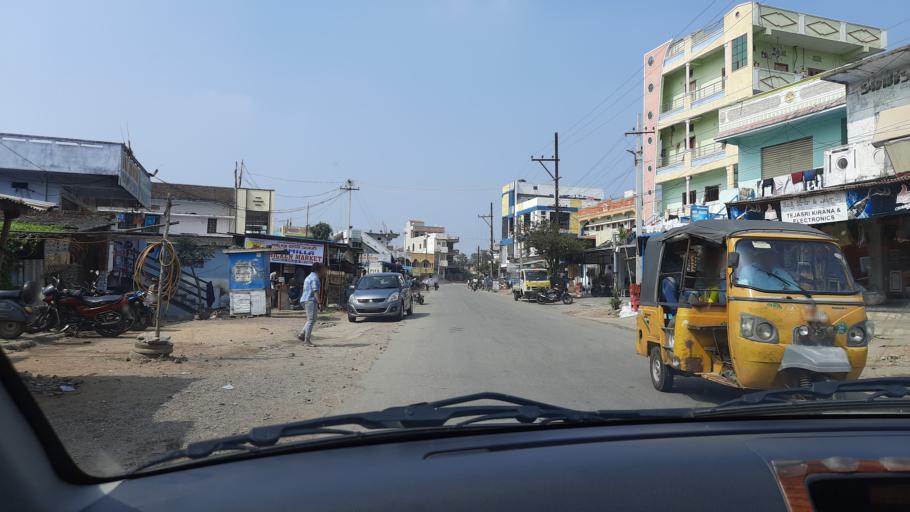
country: IN
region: Telangana
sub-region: Rangareddi
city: Lal Bahadur Nagar
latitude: 17.2709
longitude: 78.6705
